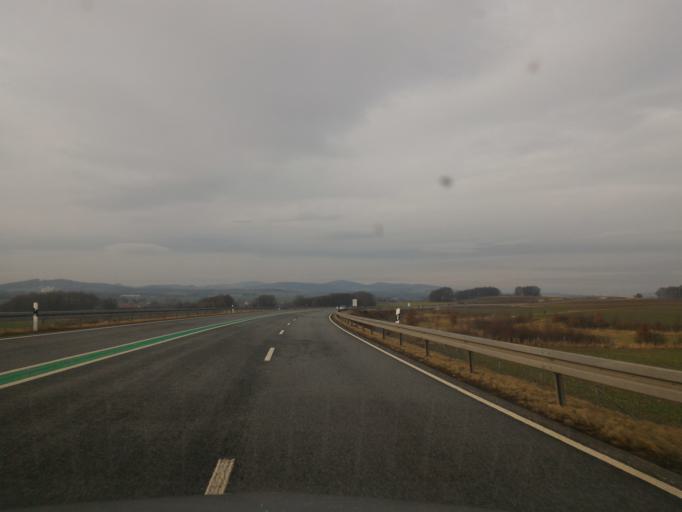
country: DE
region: Saxony
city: Niedercunnersdorf
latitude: 51.0422
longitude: 14.6792
